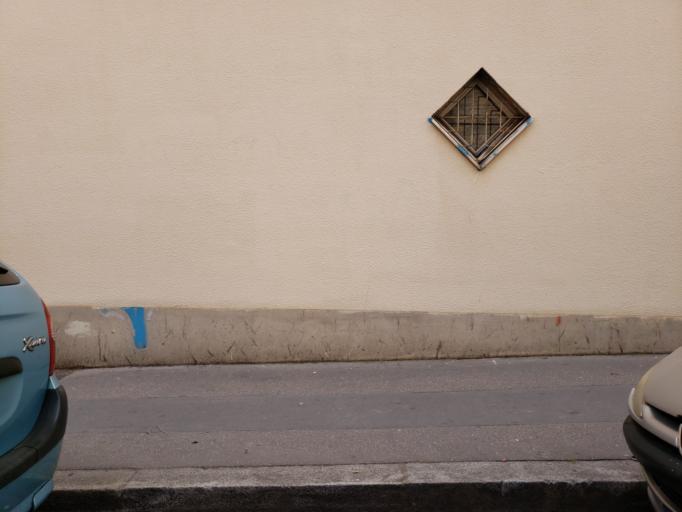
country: FR
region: Rhone-Alpes
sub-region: Departement du Rhone
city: Caluire-et-Cuire
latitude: 45.7728
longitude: 4.8326
